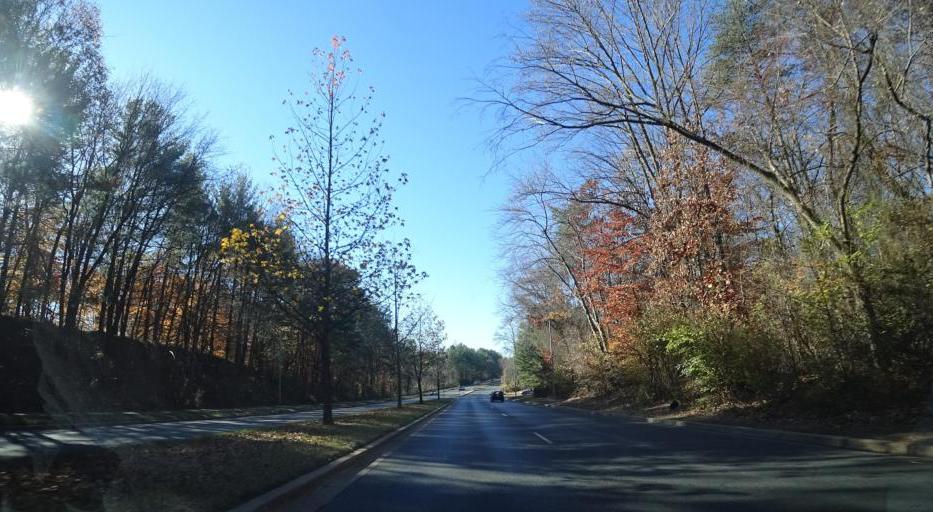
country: US
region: Maryland
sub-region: Montgomery County
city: Derwood
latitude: 39.1037
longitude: -77.1736
